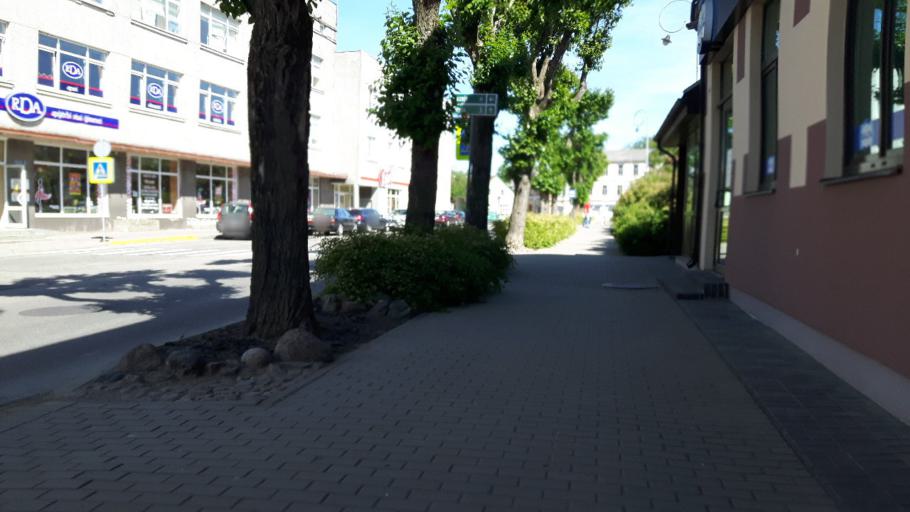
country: LV
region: Tukuma Rajons
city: Tukums
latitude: 56.9654
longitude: 23.1547
